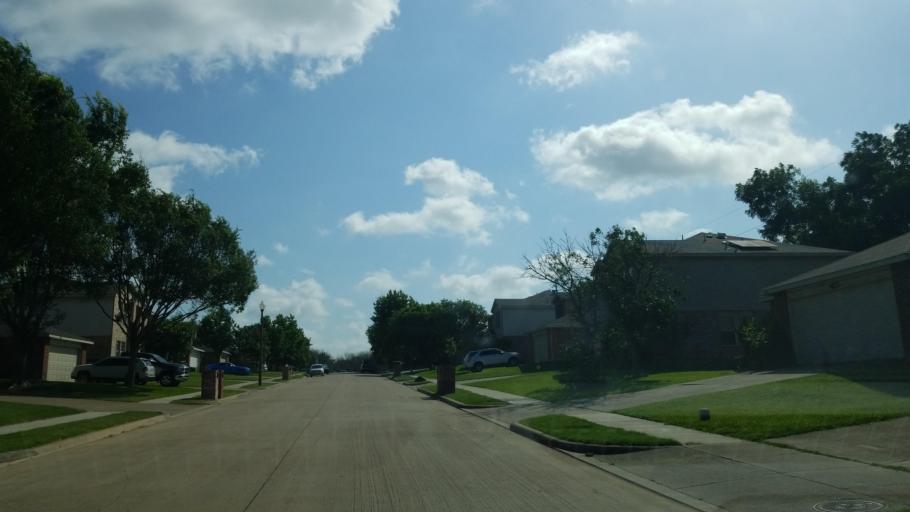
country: US
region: Texas
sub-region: Denton County
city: Copper Canyon
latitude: 33.1390
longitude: -97.1168
